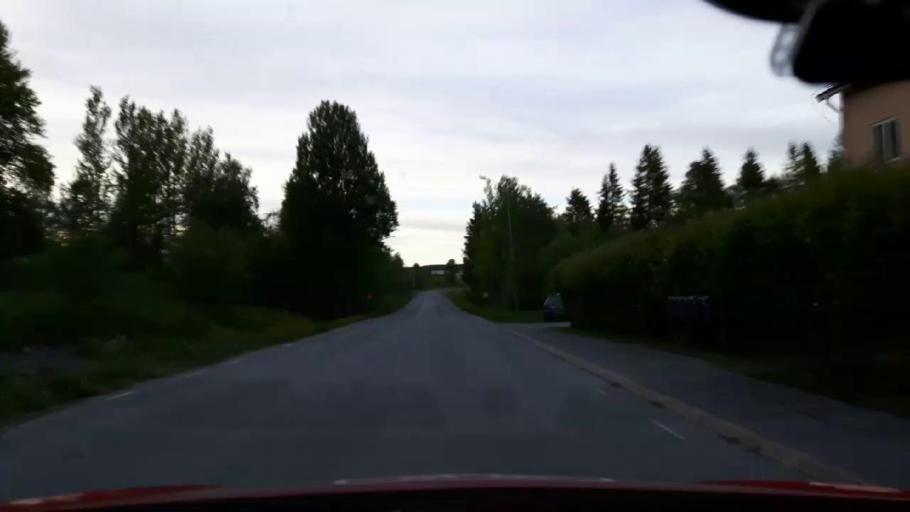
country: SE
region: Jaemtland
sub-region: OEstersunds Kommun
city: Ostersund
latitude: 62.9956
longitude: 14.5774
